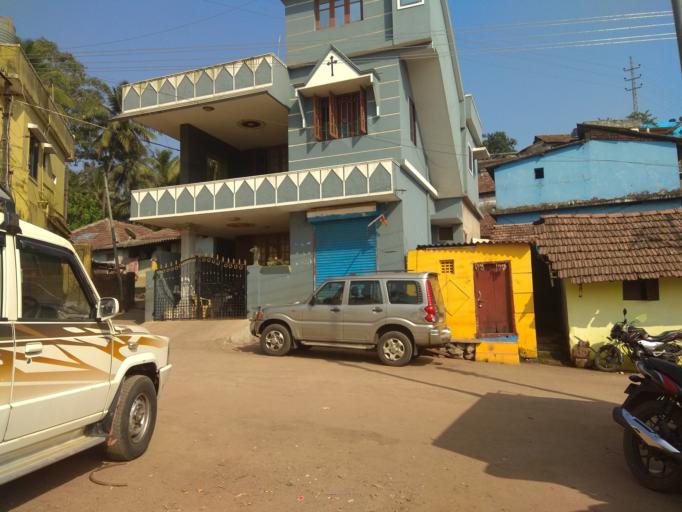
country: IN
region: Karnataka
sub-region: Dakshina Kannada
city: Mangalore
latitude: 12.9324
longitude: 74.8567
